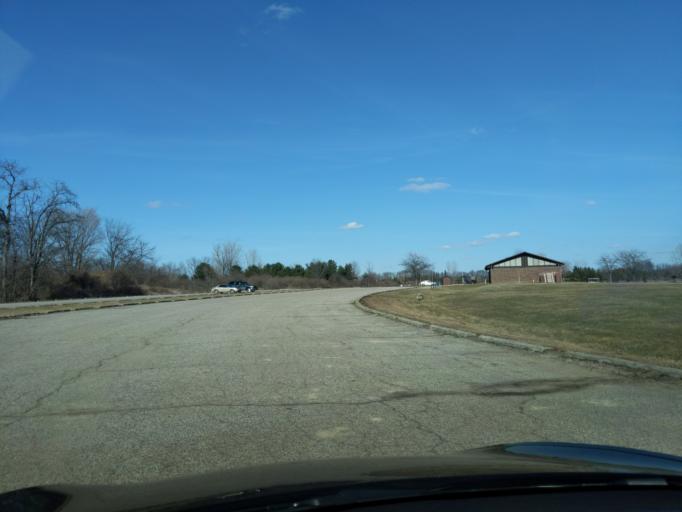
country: US
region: Michigan
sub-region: Ionia County
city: Ionia
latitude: 42.9442
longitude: -85.1333
